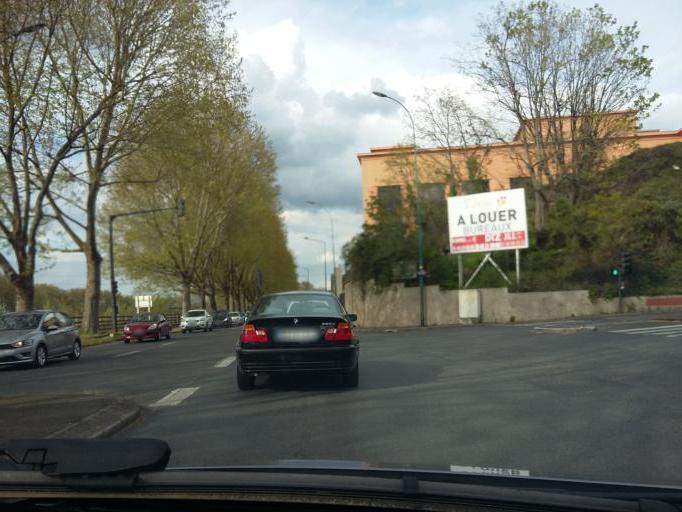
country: FR
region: Ile-de-France
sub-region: Paris
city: Saint-Ouen
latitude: 48.9225
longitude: 2.3335
